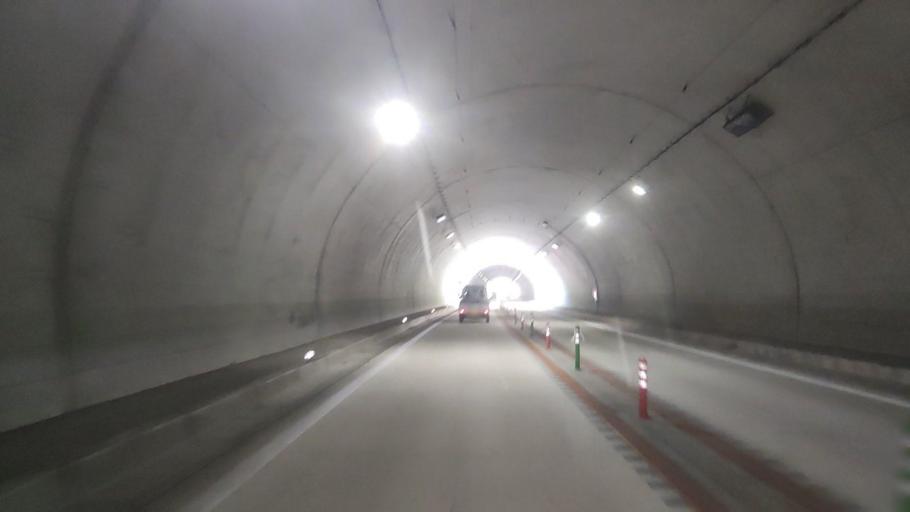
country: JP
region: Wakayama
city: Tanabe
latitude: 33.6414
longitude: 135.4096
